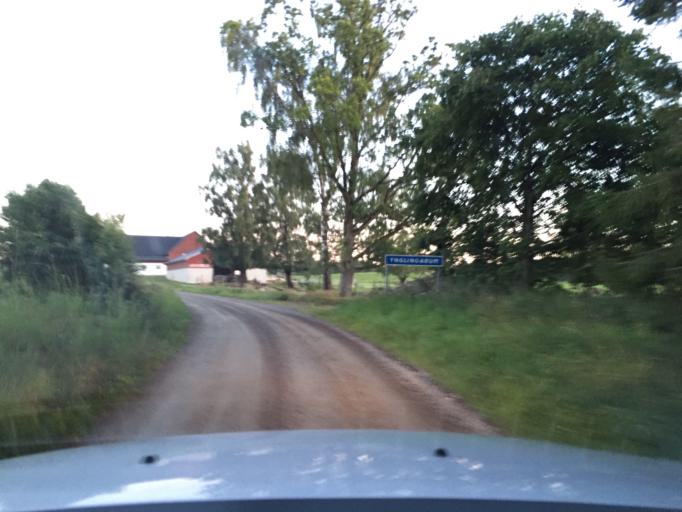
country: SE
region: Skane
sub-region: Hassleholms Kommun
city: Sosdala
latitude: 55.9854
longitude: 13.6775
